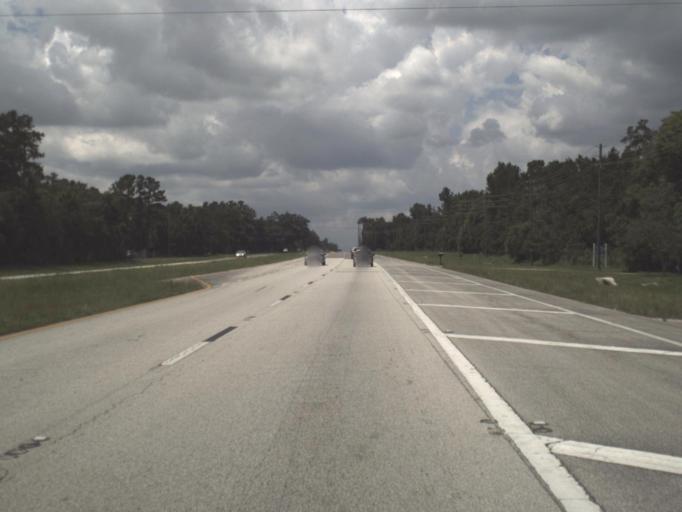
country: US
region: Florida
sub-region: Hernando County
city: South Brooksville
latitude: 28.4891
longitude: -82.4309
